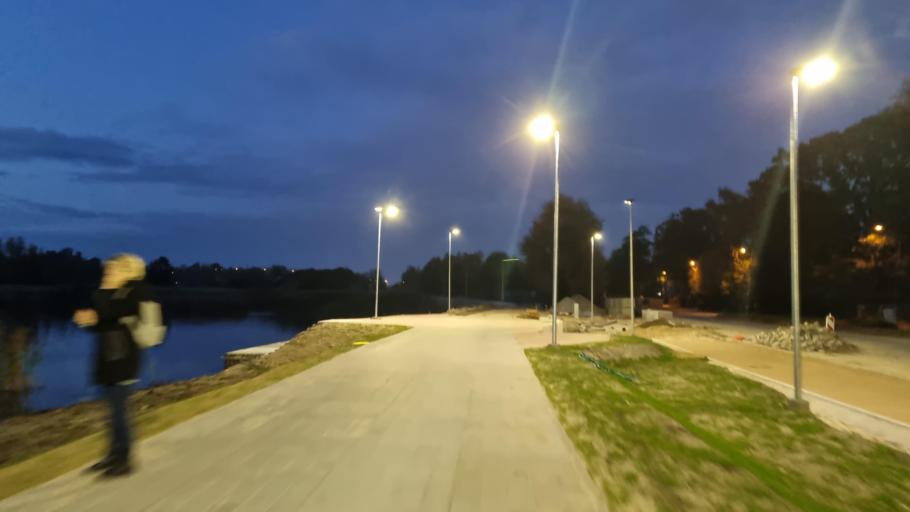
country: LV
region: Riga
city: Daugavgriva
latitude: 57.0333
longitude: 24.0360
